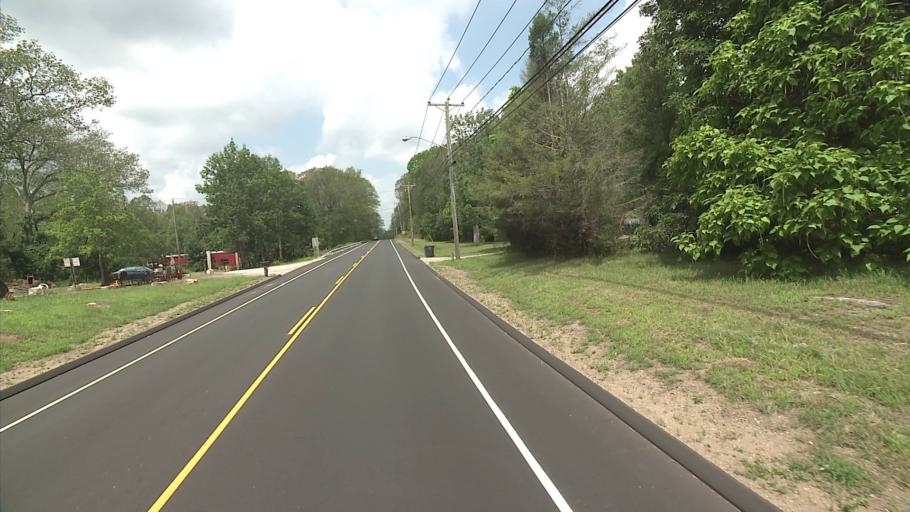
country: US
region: Connecticut
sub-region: New London County
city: Jewett City
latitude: 41.5767
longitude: -71.8866
